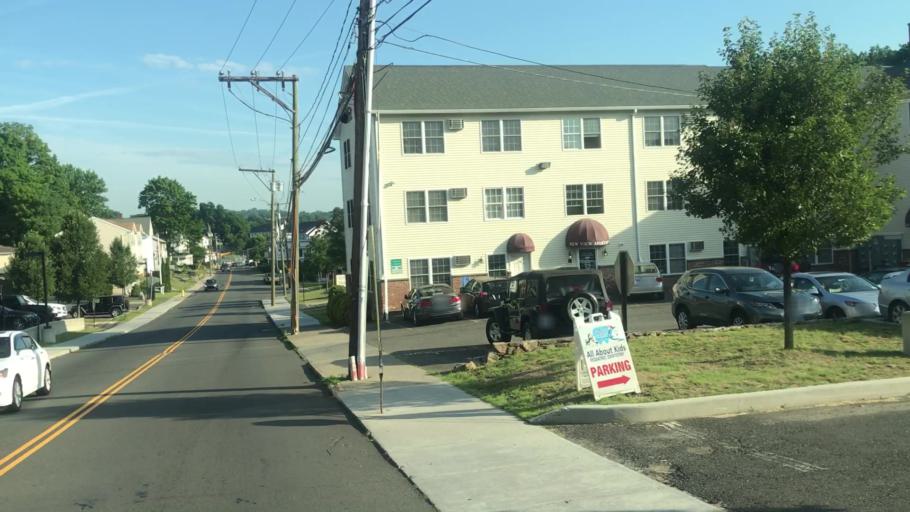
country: US
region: Connecticut
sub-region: Fairfield County
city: Danbury
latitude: 41.3926
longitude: -73.4547
